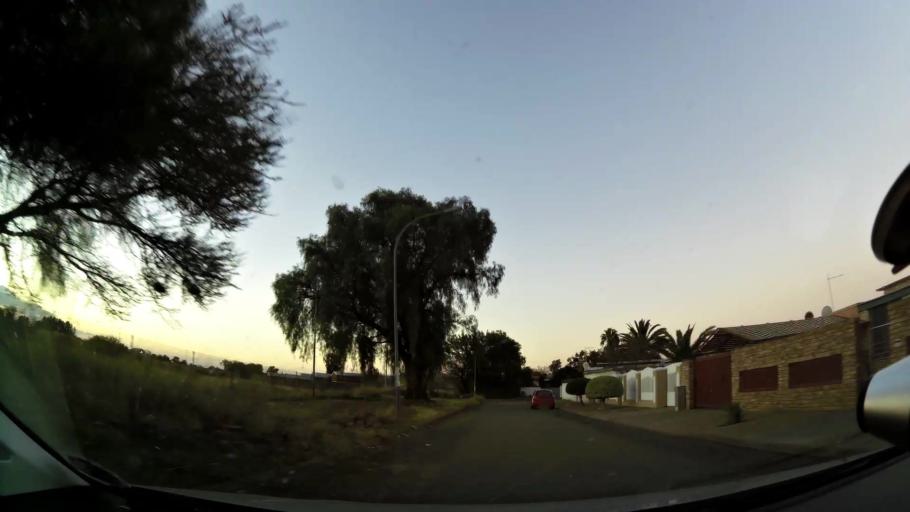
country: ZA
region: Northern Cape
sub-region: Frances Baard District Municipality
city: Kimberley
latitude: -28.7266
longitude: 24.7650
